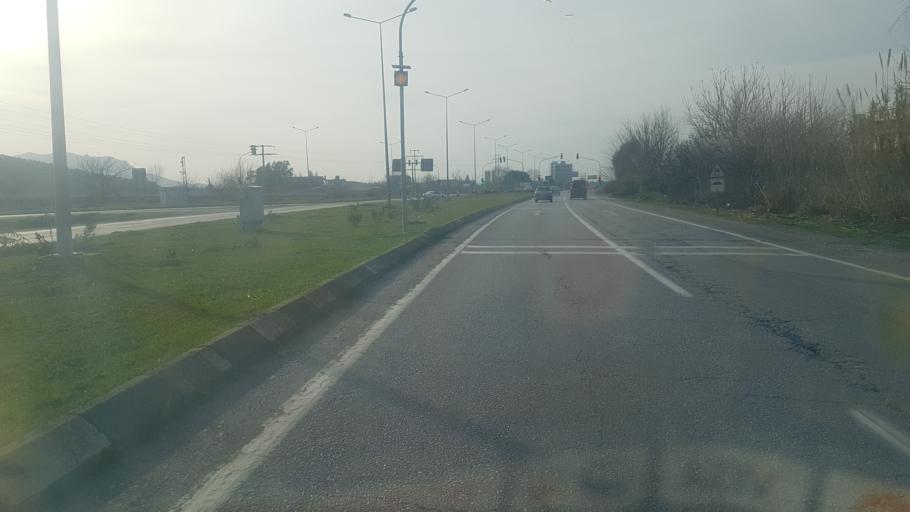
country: TR
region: Osmaniye
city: Toprakkale
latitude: 37.0566
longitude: 36.1233
